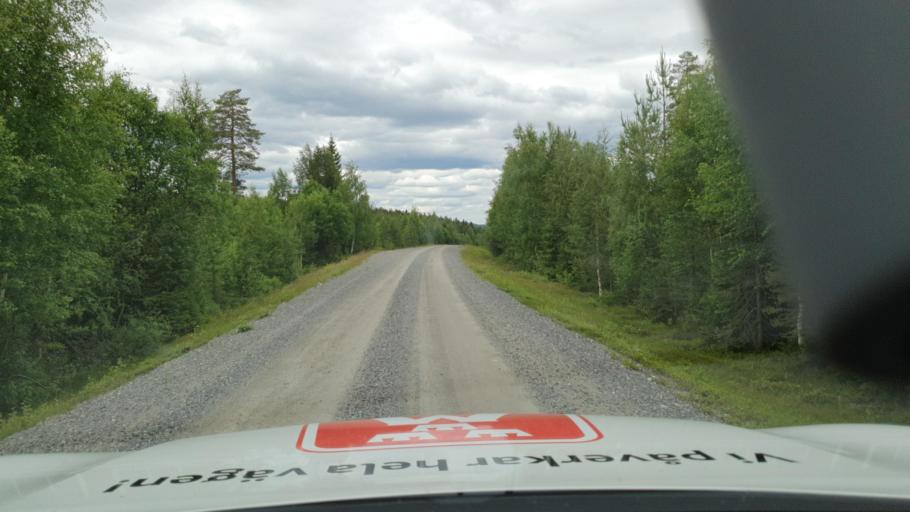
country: SE
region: Vaesterbotten
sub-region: Nordmalings Kommun
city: Nordmaling
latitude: 63.7479
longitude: 19.3775
